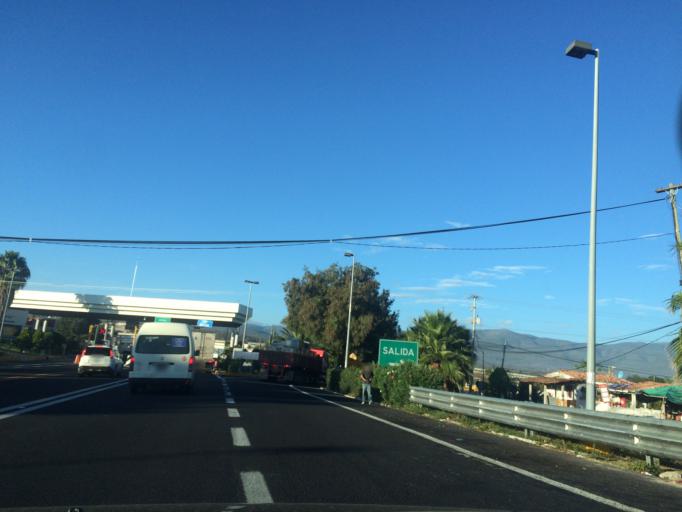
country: MX
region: Puebla
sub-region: Santiago Miahuatlan
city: San Jose Monte Chiquito
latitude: 18.4881
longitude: -97.4561
